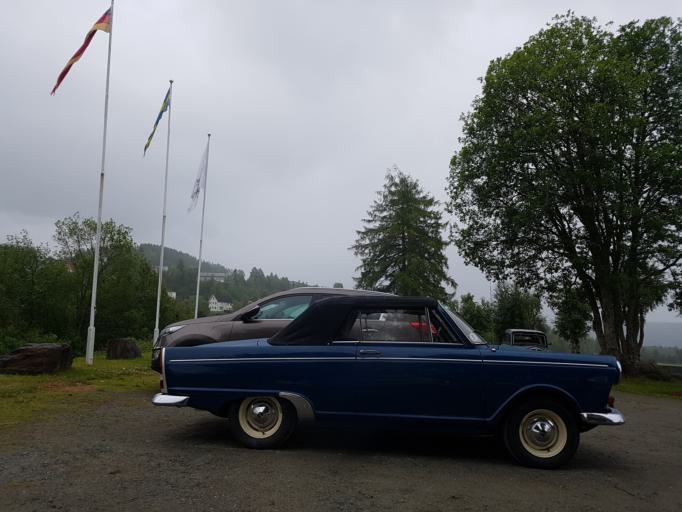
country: NO
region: Sor-Trondelag
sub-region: Selbu
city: Mebonden
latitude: 63.2328
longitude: 11.0302
